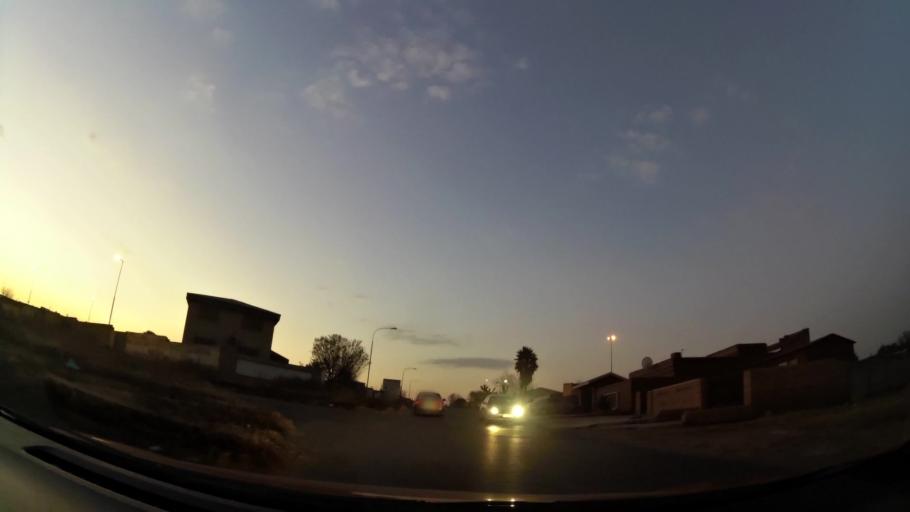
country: ZA
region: Gauteng
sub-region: City of Johannesburg Metropolitan Municipality
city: Soweto
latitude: -26.2300
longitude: 27.9116
